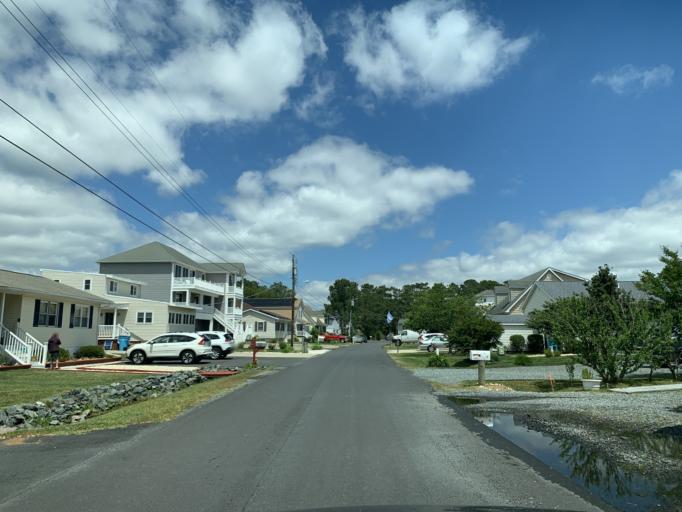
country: US
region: Maryland
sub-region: Worcester County
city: West Ocean City
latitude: 38.3573
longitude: -75.1180
